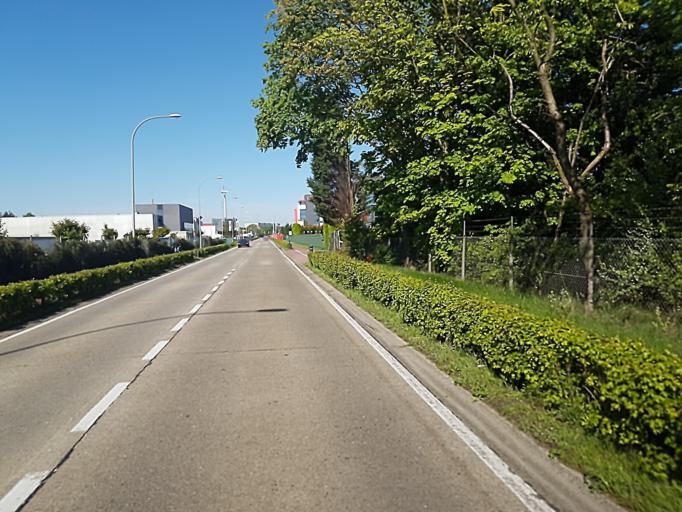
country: BE
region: Flanders
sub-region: Provincie Antwerpen
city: Turnhout
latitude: 51.3003
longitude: 4.9443
